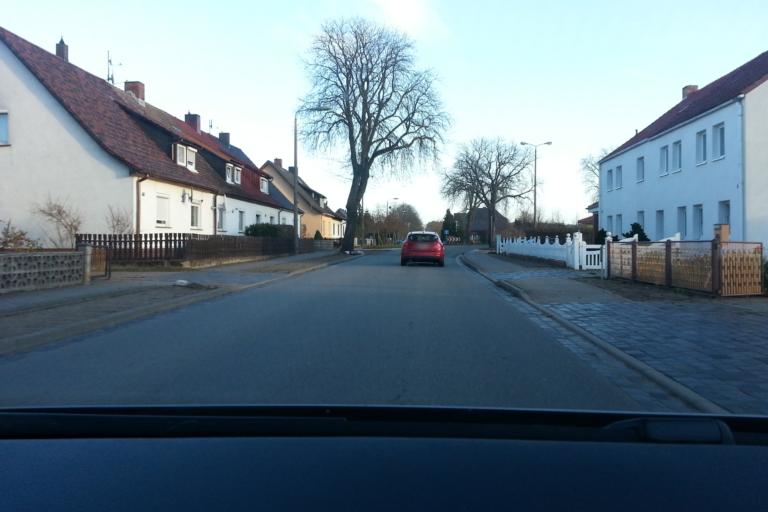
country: DE
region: Mecklenburg-Vorpommern
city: Ferdinandshof
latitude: 53.6631
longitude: 13.8968
